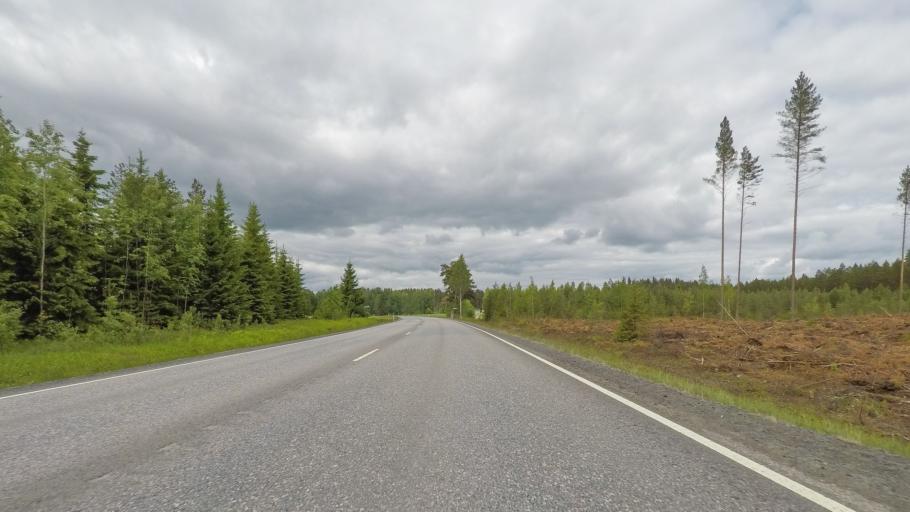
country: FI
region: Central Finland
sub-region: Joutsa
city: Joutsa
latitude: 61.6914
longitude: 26.0591
